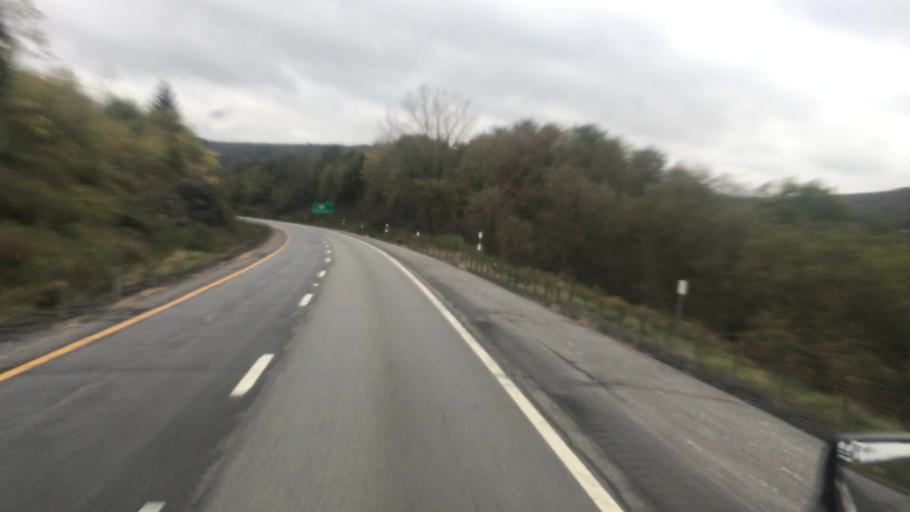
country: US
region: New York
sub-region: Chenango County
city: Bainbridge
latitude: 42.2947
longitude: -75.4625
